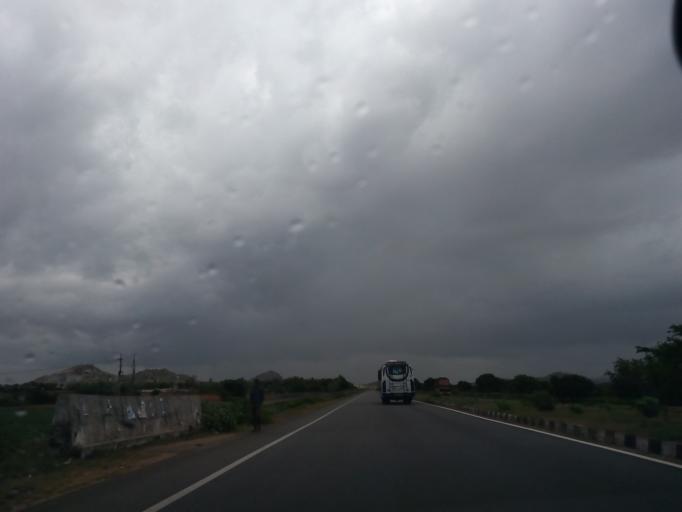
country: IN
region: Karnataka
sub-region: Chitradurga
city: Chitradurga
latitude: 14.2696
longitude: 76.3302
